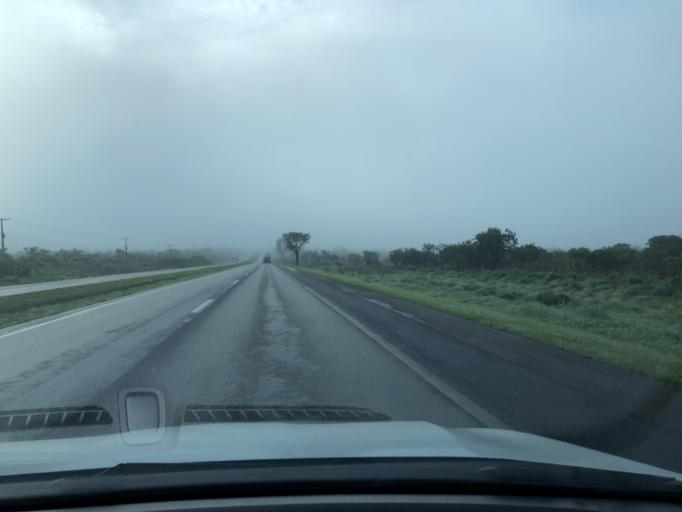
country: BR
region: Goias
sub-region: Luziania
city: Luziania
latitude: -16.2929
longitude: -47.8515
